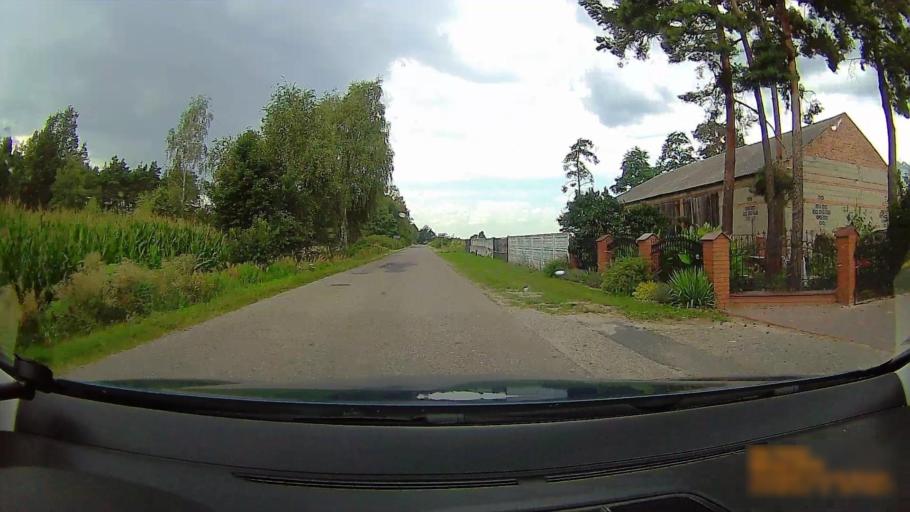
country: PL
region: Greater Poland Voivodeship
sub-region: Powiat koninski
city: Rychwal
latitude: 52.1041
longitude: 18.1982
